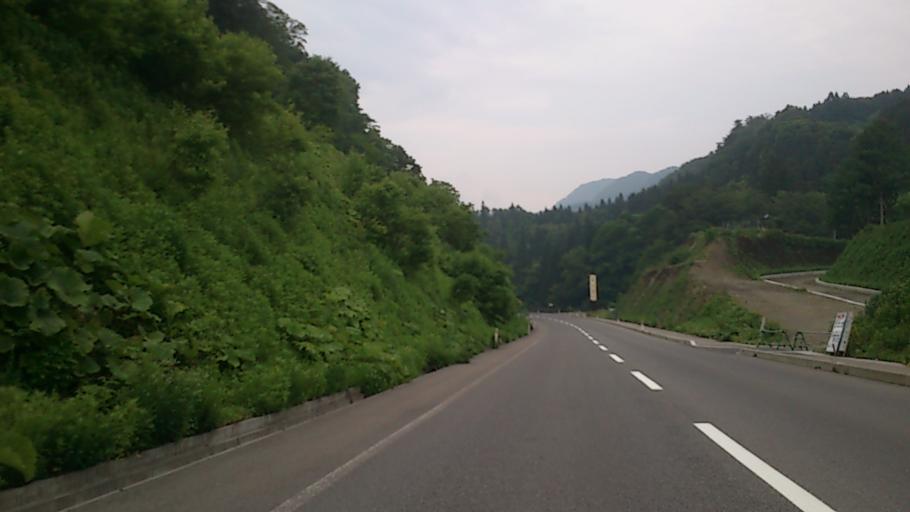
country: JP
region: Aomori
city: Hirosaki
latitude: 40.5715
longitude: 140.2972
